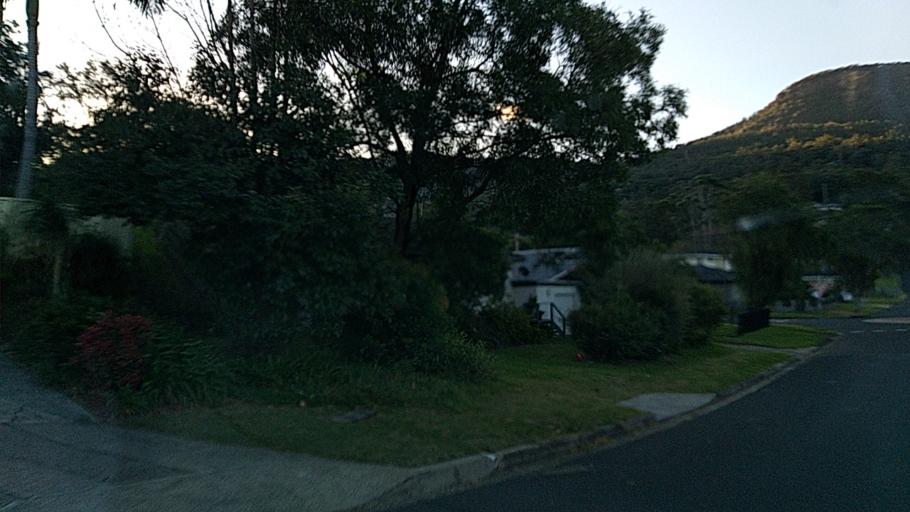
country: AU
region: New South Wales
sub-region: Wollongong
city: Mount Keira
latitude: -34.4191
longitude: 150.8554
